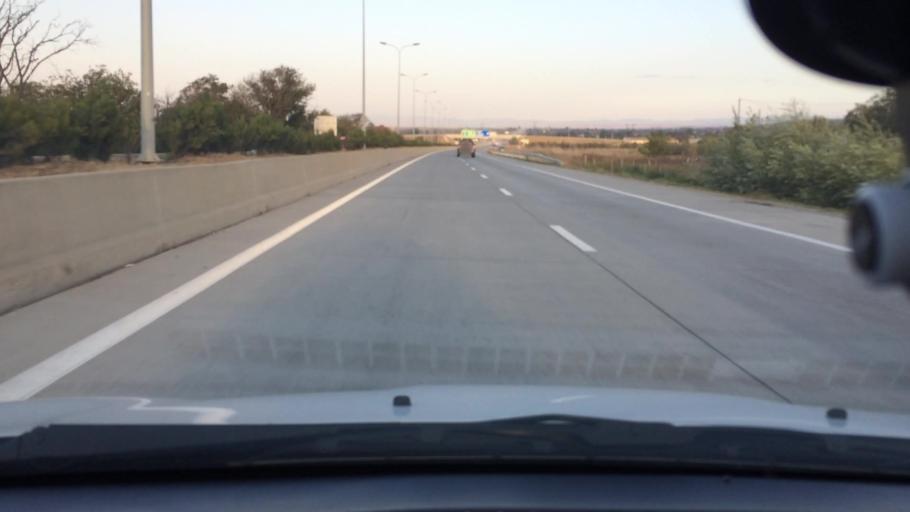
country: GE
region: Shida Kartli
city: Gori
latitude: 42.0183
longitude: 43.9866
